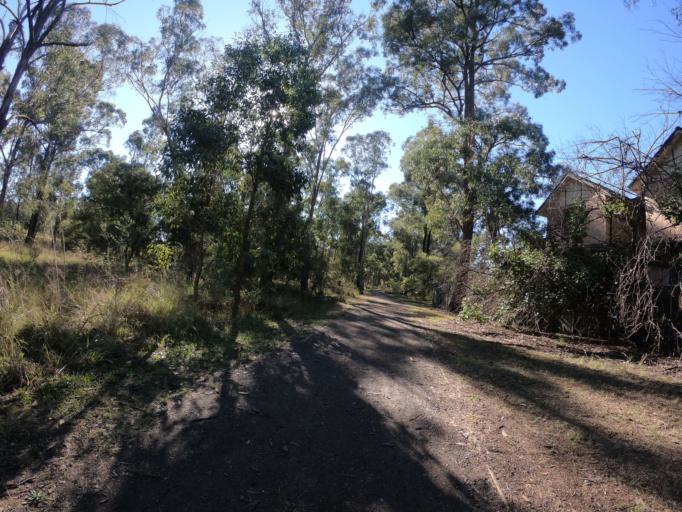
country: AU
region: New South Wales
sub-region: Hawkesbury
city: South Windsor
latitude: -33.6336
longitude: 150.7904
